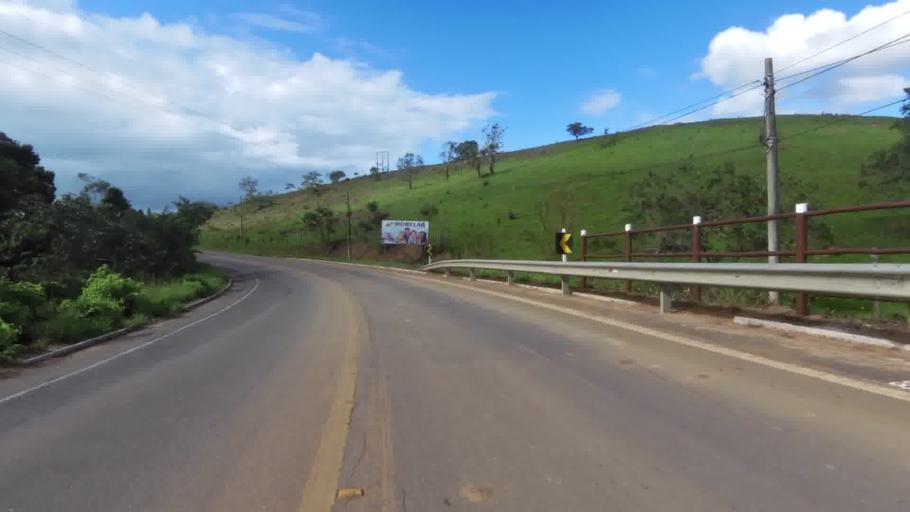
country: BR
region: Espirito Santo
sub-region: Piuma
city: Piuma
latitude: -20.8836
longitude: -40.7679
